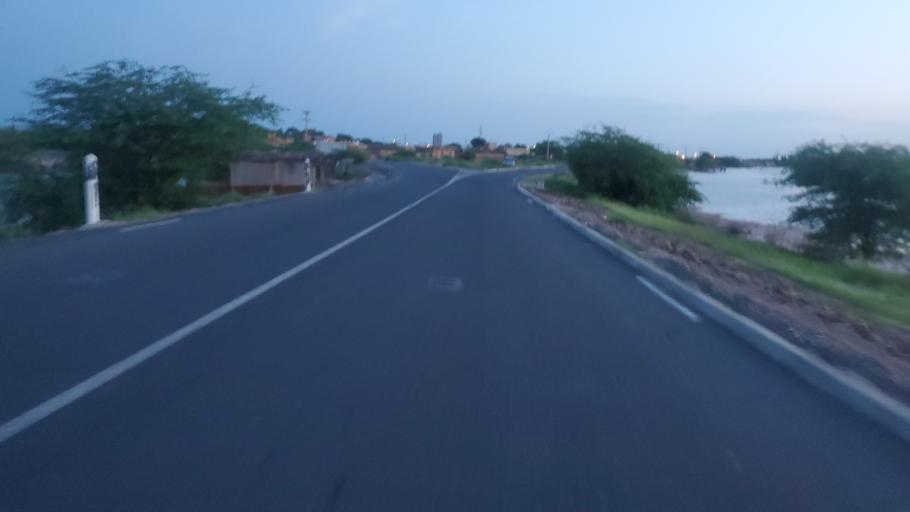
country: SN
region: Saint-Louis
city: Saint-Louis
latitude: 16.0728
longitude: -16.3892
